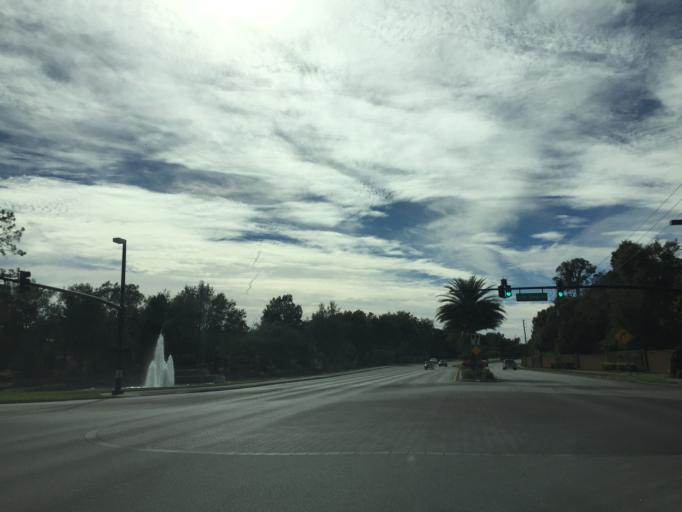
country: US
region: Florida
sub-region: Seminole County
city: Winter Springs
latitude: 28.6758
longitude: -81.2701
